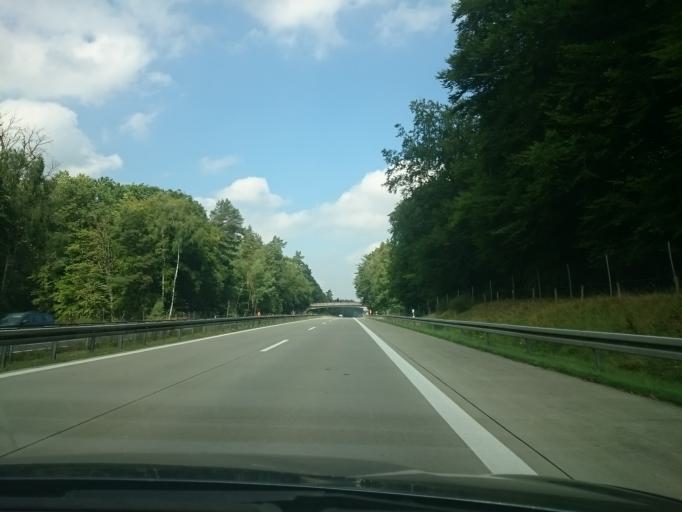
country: DE
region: Brandenburg
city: Althuttendorf
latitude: 53.0451
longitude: 13.8347
